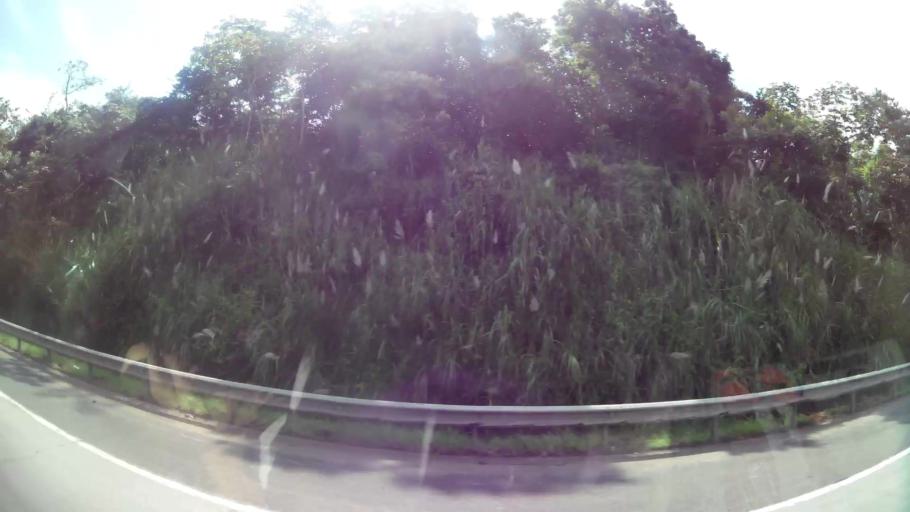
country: PA
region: Panama
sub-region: Distrito de Panama
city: Paraiso
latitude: 9.0328
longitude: -79.6157
